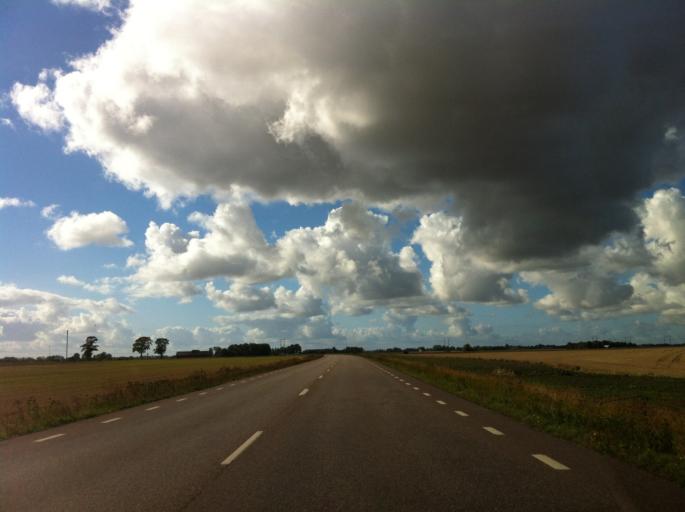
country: SE
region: Skane
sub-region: Lunds Kommun
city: Lund
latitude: 55.7930
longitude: 13.2131
